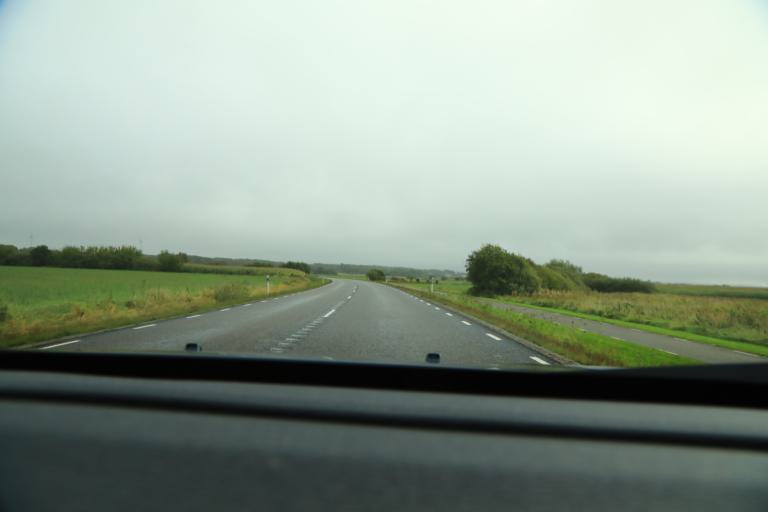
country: SE
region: Halland
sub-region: Varbergs Kommun
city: Traslovslage
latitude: 57.0477
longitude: 12.3310
